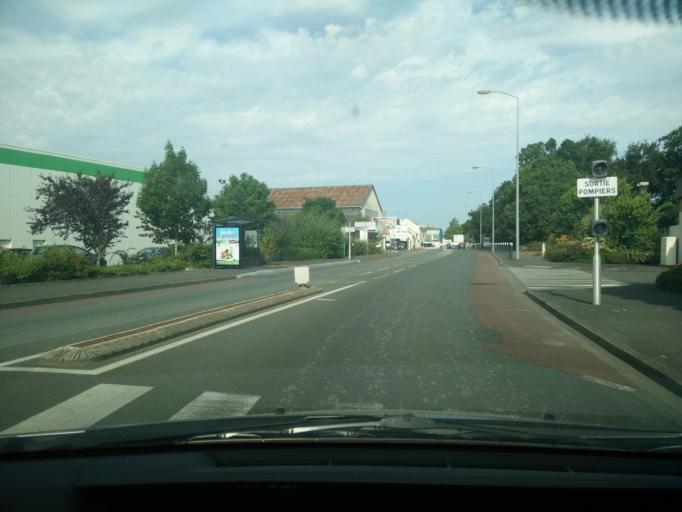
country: FR
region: Pays de la Loire
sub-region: Departement de Maine-et-Loire
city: Angers
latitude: 47.4704
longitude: -0.5162
